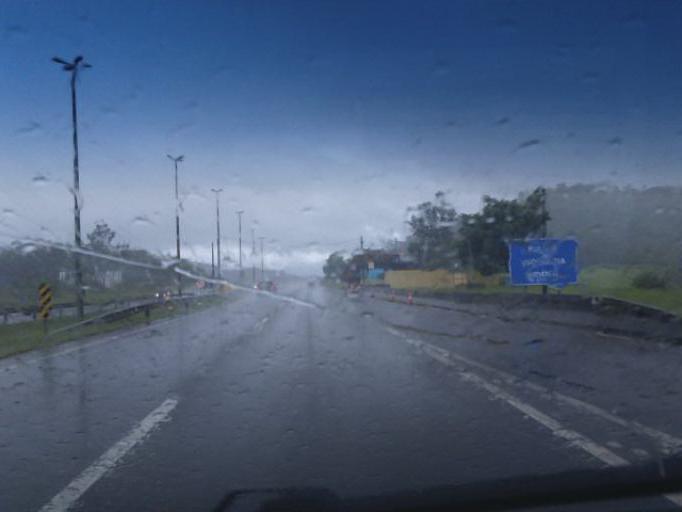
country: BR
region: Sao Paulo
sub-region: Miracatu
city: Miracatu
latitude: -24.2678
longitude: -47.3940
